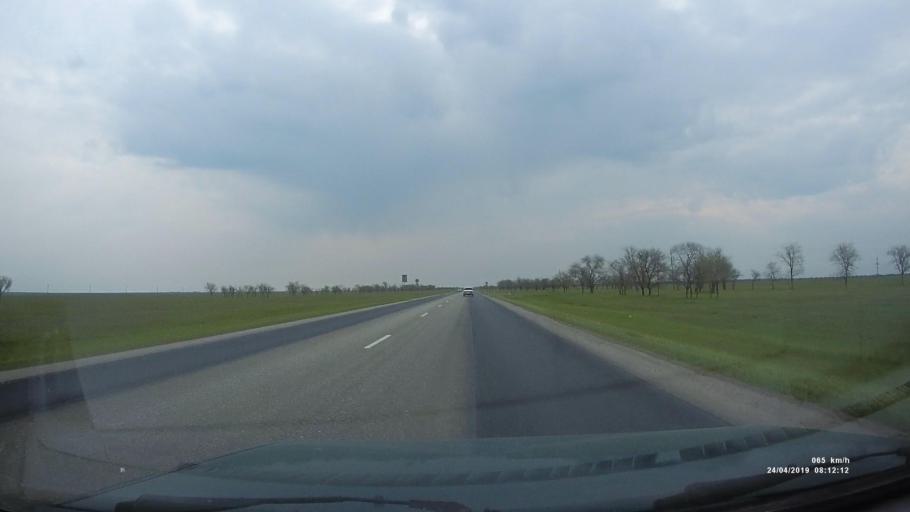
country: RU
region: Kalmykiya
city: Priyutnoye
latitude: 46.1032
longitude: 43.5377
